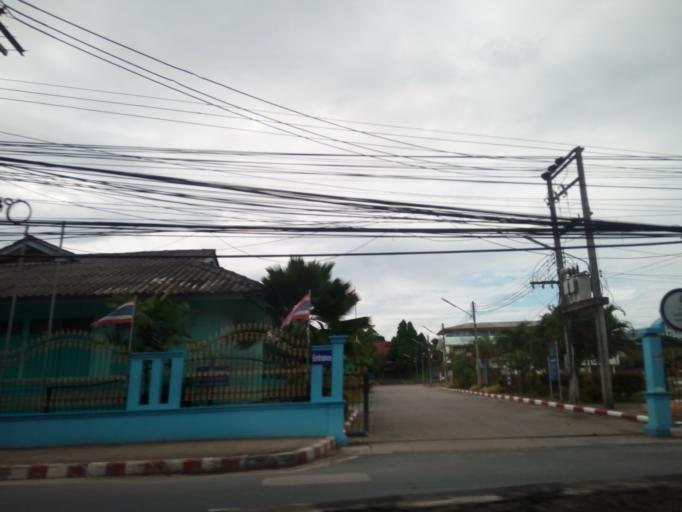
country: TH
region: Phuket
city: Wichit
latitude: 7.8863
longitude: 98.3648
